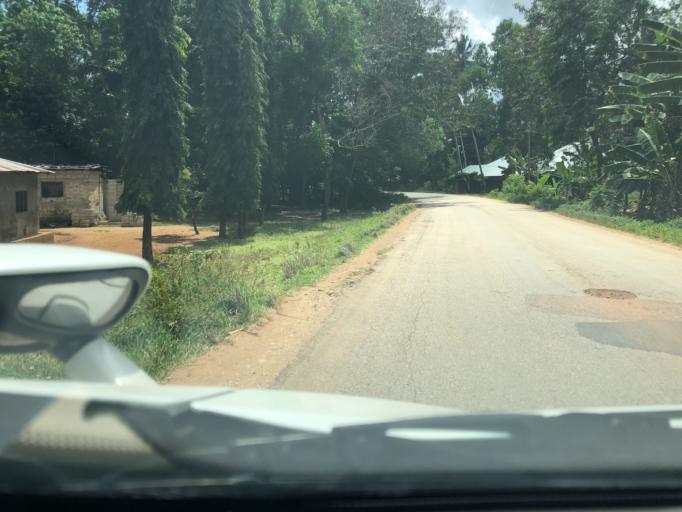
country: TZ
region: Zanzibar Central/South
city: Koani
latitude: -6.0675
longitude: 39.2508
